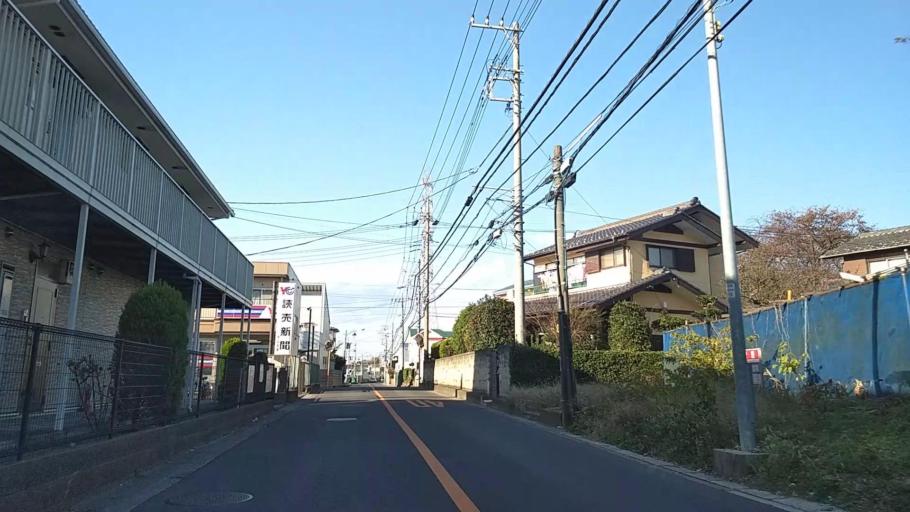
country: JP
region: Tokyo
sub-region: Machida-shi
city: Machida
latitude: 35.5318
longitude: 139.5472
